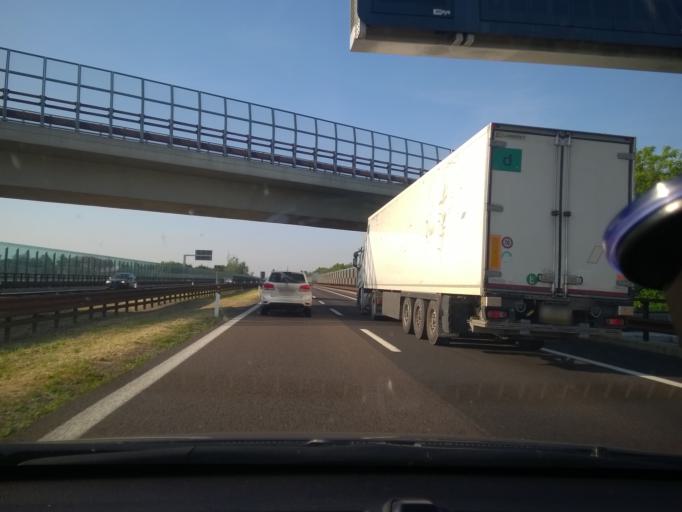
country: IT
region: Emilia-Romagna
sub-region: Provincia di Modena
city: Santa Croce Scuole
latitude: 44.7556
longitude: 10.8440
